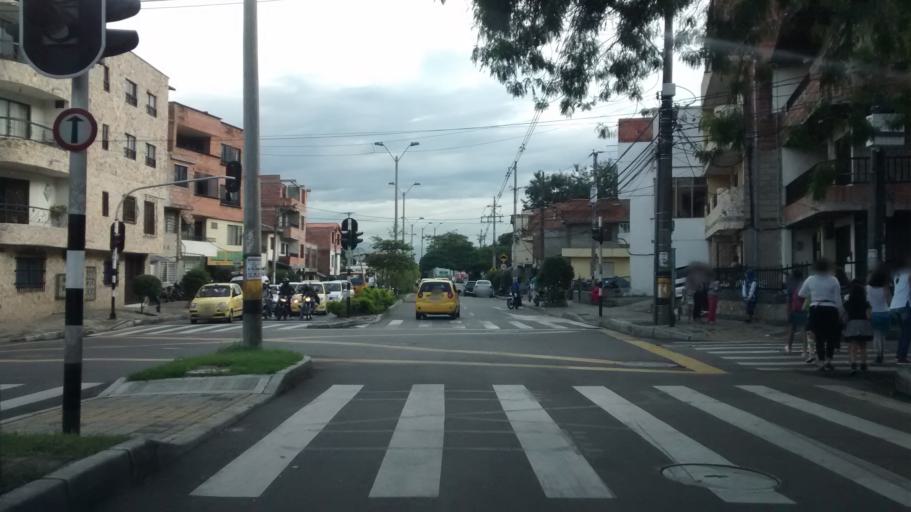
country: CO
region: Antioquia
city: Bello
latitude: 6.2993
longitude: -75.5667
